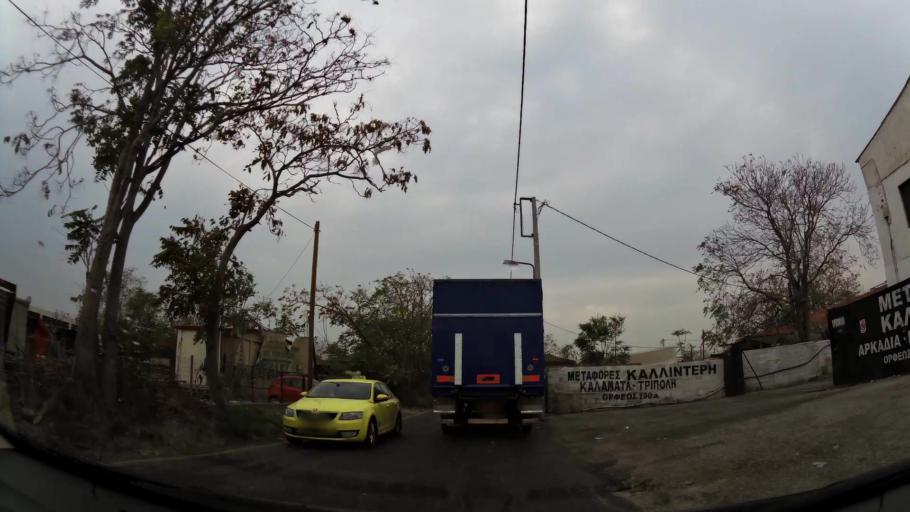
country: GR
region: Attica
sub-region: Nomarchia Athinas
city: Aigaleo
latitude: 37.9809
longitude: 23.6906
